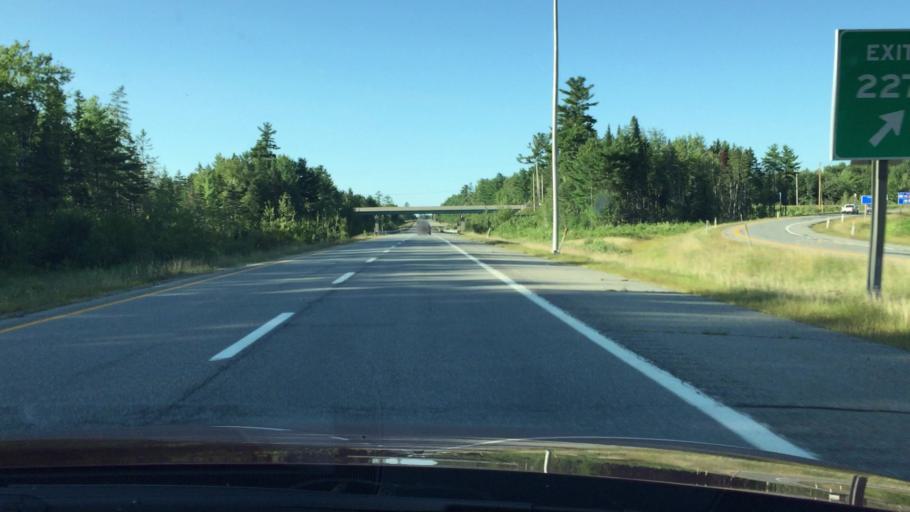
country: US
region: Maine
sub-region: Penobscot County
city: Lincoln
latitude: 45.3730
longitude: -68.6047
